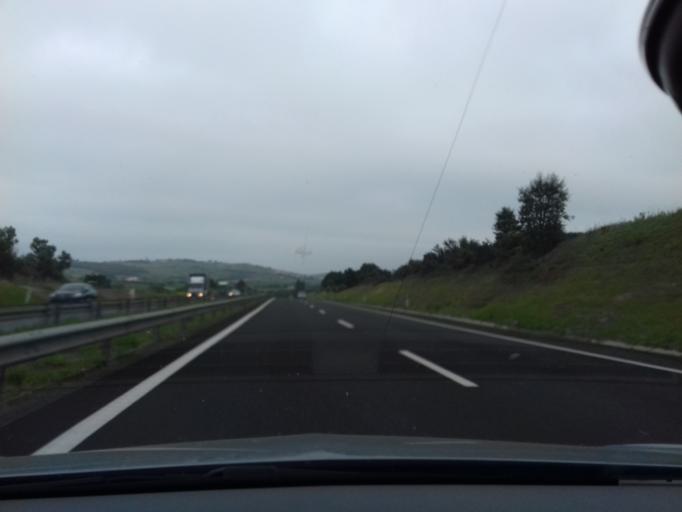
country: PT
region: Leiria
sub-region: Bombarral
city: Bombarral
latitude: 39.2669
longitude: -9.1661
